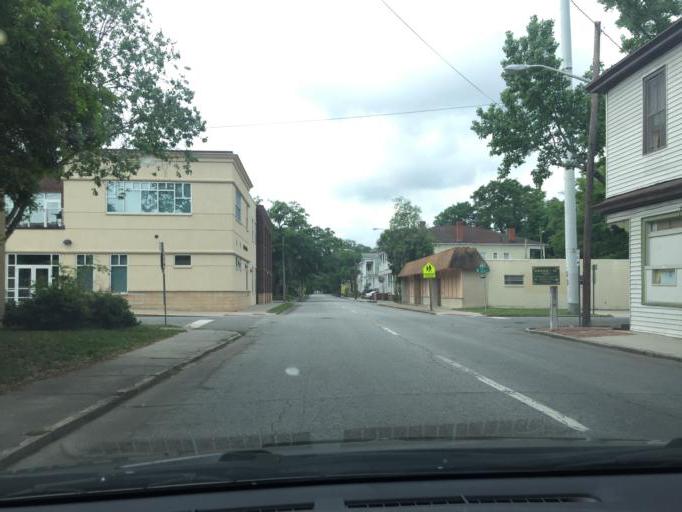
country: US
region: Georgia
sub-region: Chatham County
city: Savannah
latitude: 32.0614
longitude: -81.0998
